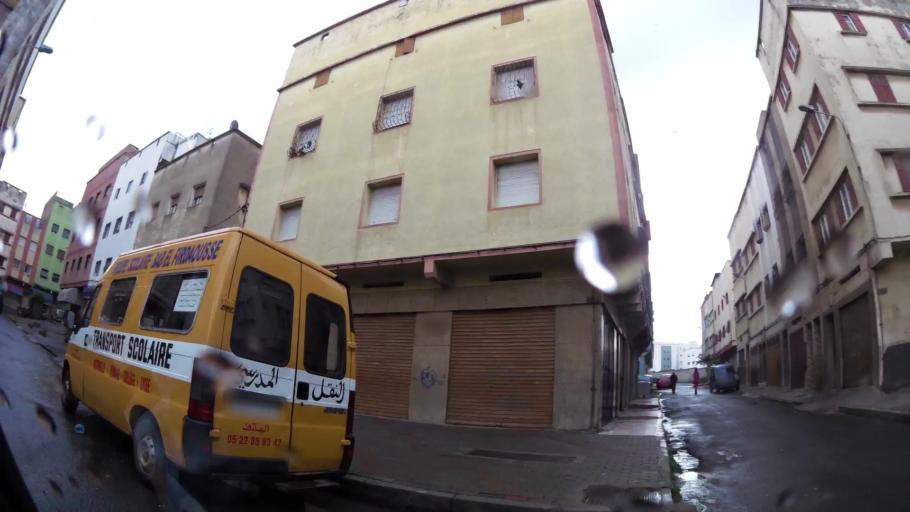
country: MA
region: Grand Casablanca
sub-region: Casablanca
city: Casablanca
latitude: 33.5515
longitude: -7.5847
